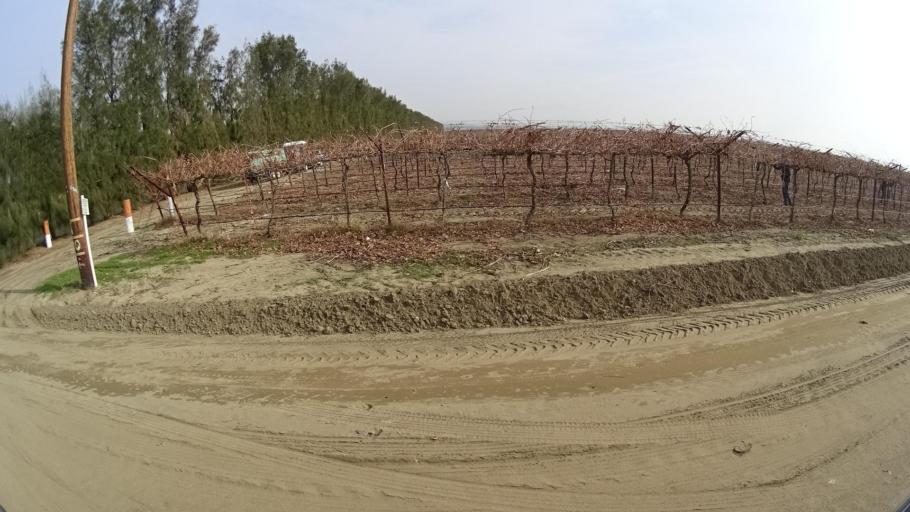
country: US
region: California
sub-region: Kern County
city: Arvin
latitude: 35.0998
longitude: -118.8505
